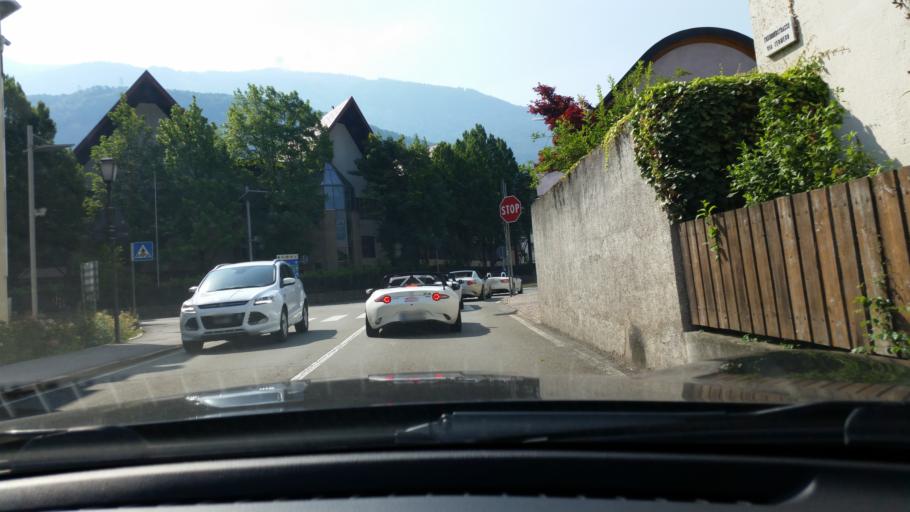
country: IT
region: Trentino-Alto Adige
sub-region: Bolzano
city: Ora
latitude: 46.3465
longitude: 11.2952
